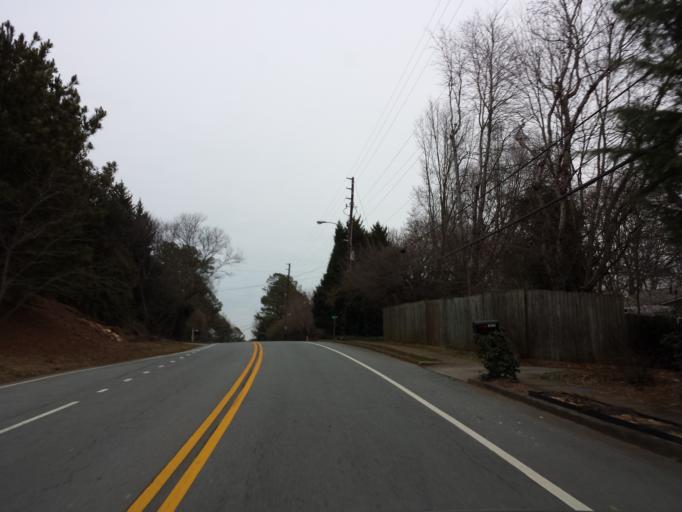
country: US
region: Georgia
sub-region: Fulton County
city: Roswell
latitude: 34.0186
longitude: -84.3768
